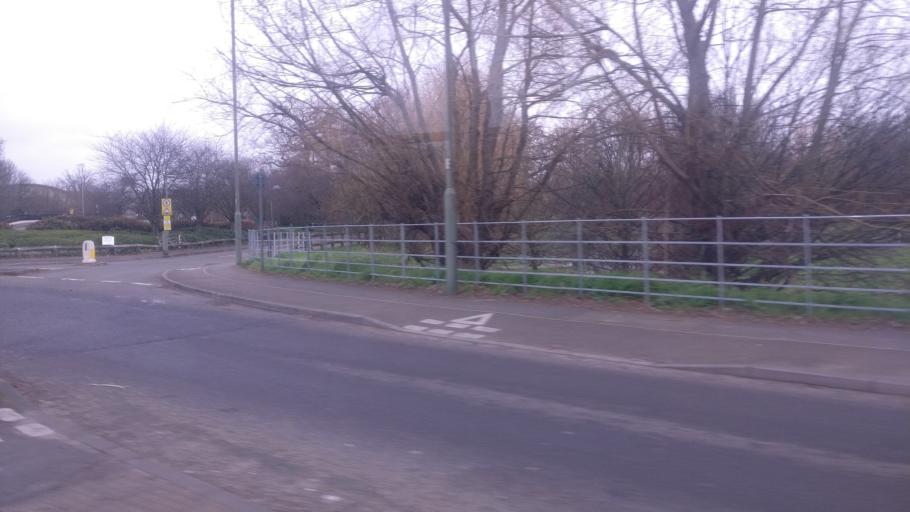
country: GB
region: England
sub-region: Surrey
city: Chertsey
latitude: 51.3869
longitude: -0.5049
